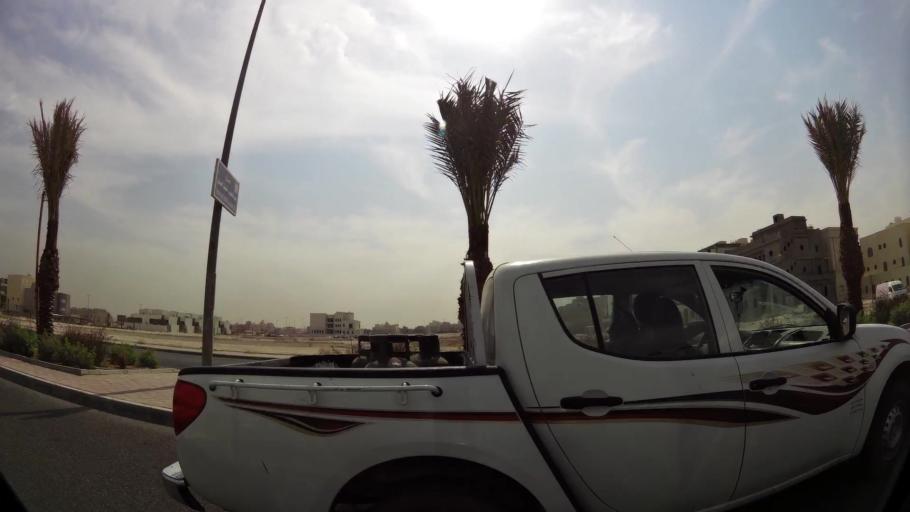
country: KW
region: Al Farwaniyah
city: Janub as Surrah
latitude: 29.2898
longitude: 47.9913
